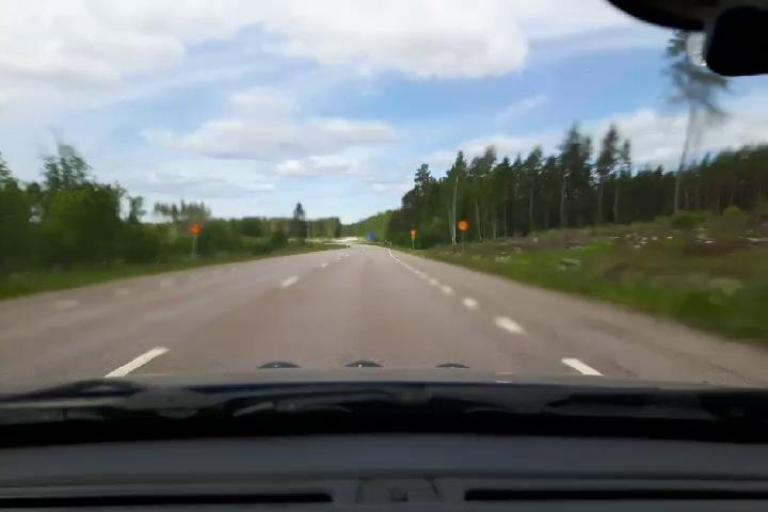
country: SE
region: Uppsala
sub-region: Tierps Kommun
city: Tierp
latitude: 60.3542
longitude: 17.4537
